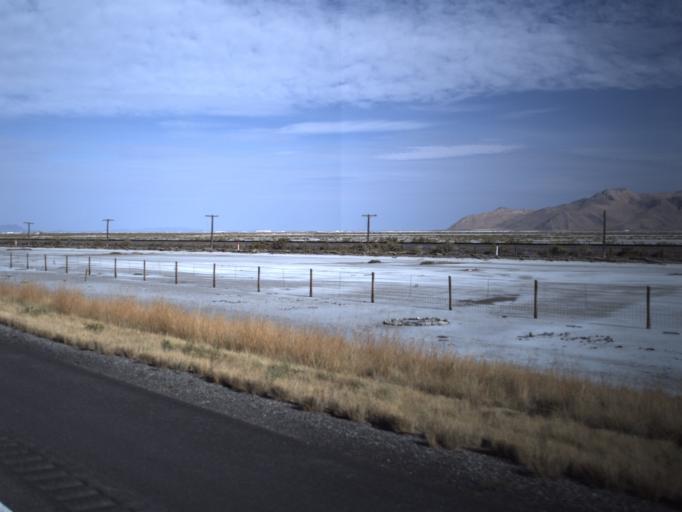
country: US
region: Utah
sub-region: Tooele County
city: Grantsville
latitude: 40.6990
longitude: -112.4825
